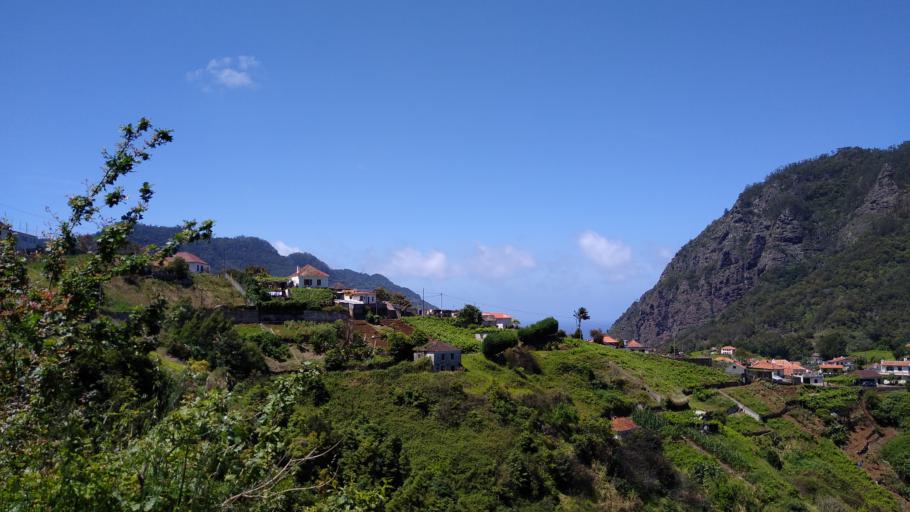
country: PT
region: Madeira
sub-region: Santana
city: Santana
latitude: 32.7651
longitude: -16.8442
